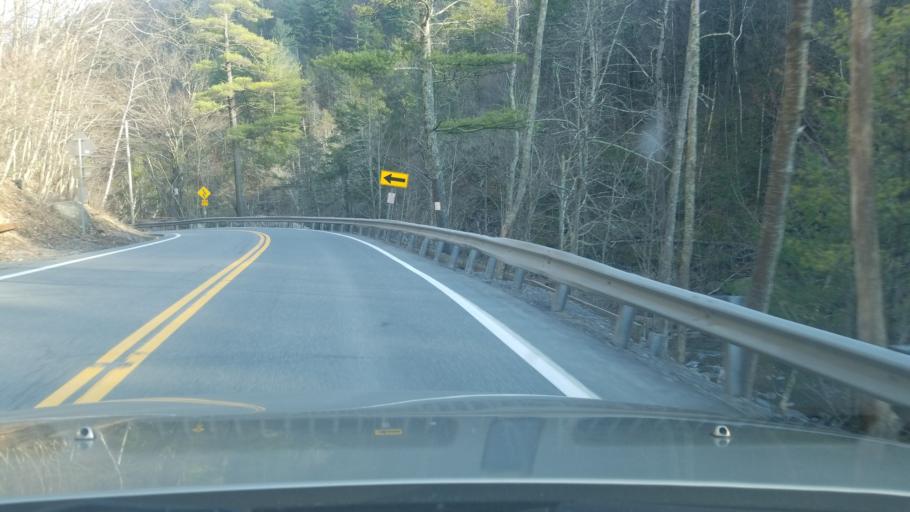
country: US
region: New York
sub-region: Greene County
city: Palenville
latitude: 42.1777
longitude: -74.0581
